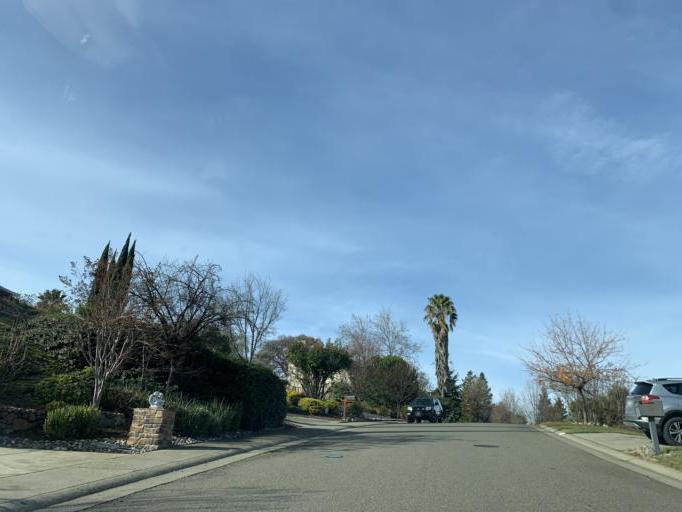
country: US
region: California
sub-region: El Dorado County
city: El Dorado Hills
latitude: 38.6529
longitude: -121.0787
